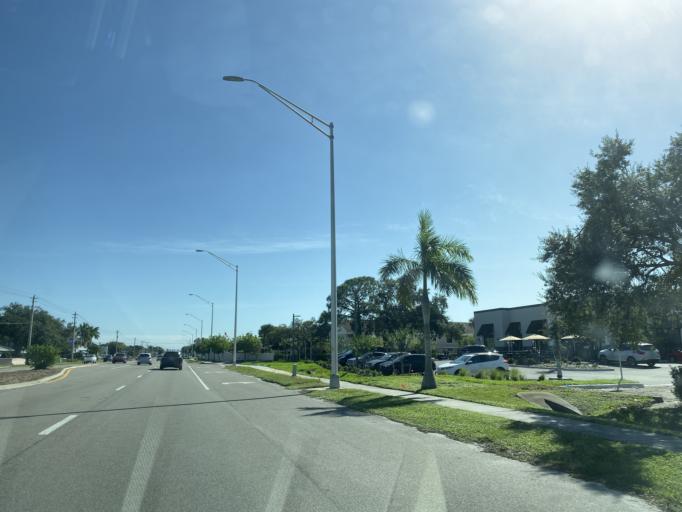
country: US
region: Florida
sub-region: Manatee County
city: West Bradenton
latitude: 27.4959
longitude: -82.6253
